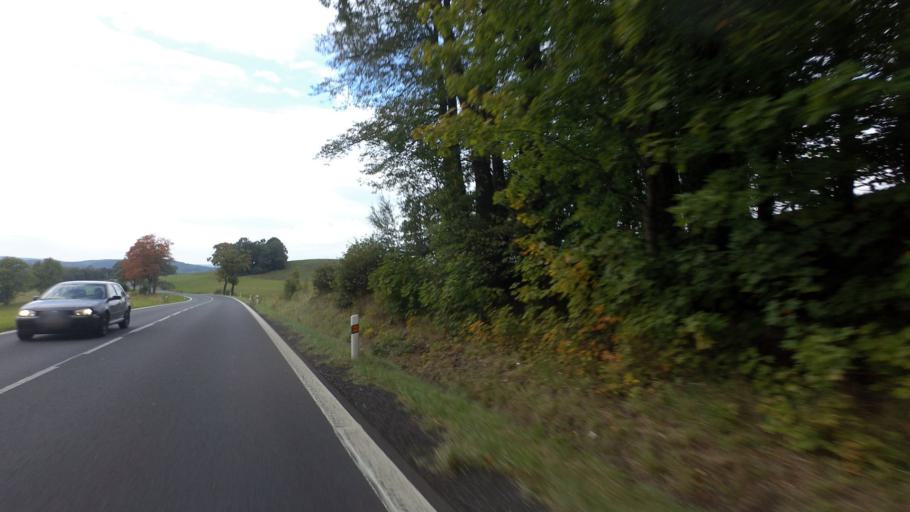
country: CZ
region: Ustecky
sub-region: Okres Decin
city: Sluknov
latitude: 50.9941
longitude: 14.4812
